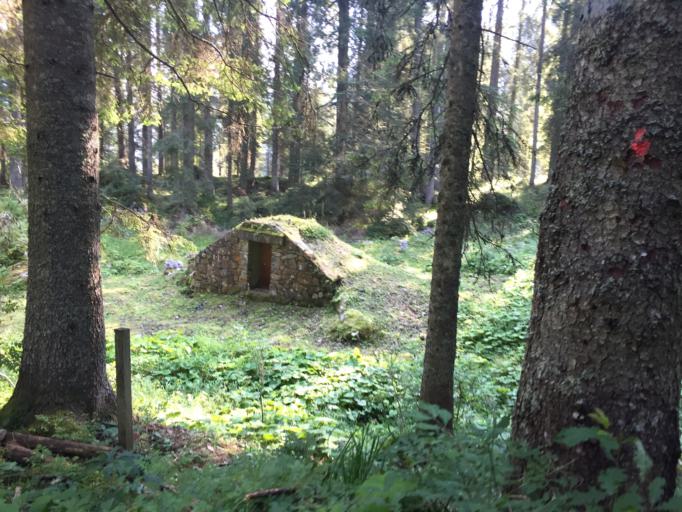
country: IT
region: Veneto
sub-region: Provincia di Belluno
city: Granvilla
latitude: 46.5583
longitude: 12.7311
